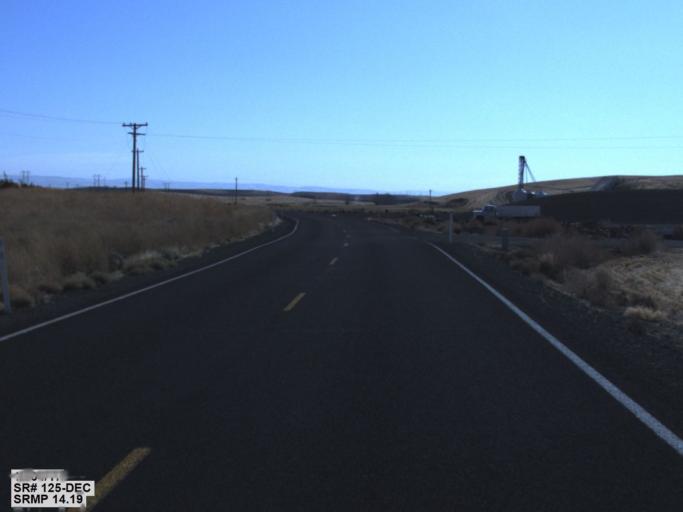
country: US
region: Washington
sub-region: Walla Walla County
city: Walla Walla
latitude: 46.1742
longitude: -118.3844
